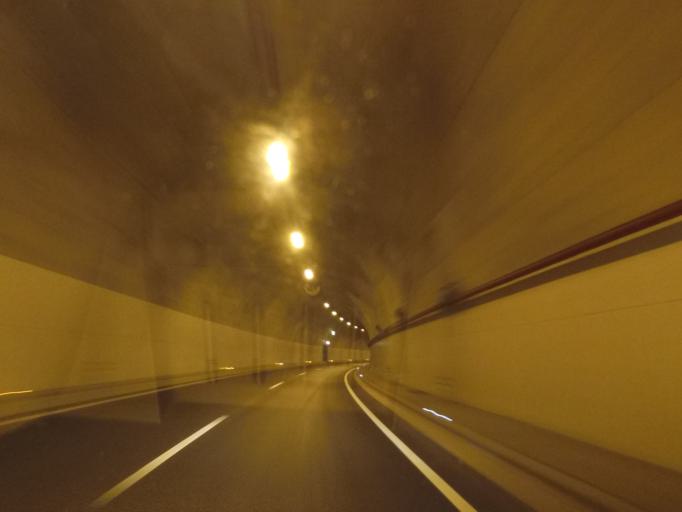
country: PT
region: Madeira
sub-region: Machico
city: Canical
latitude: 32.7448
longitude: -16.7418
